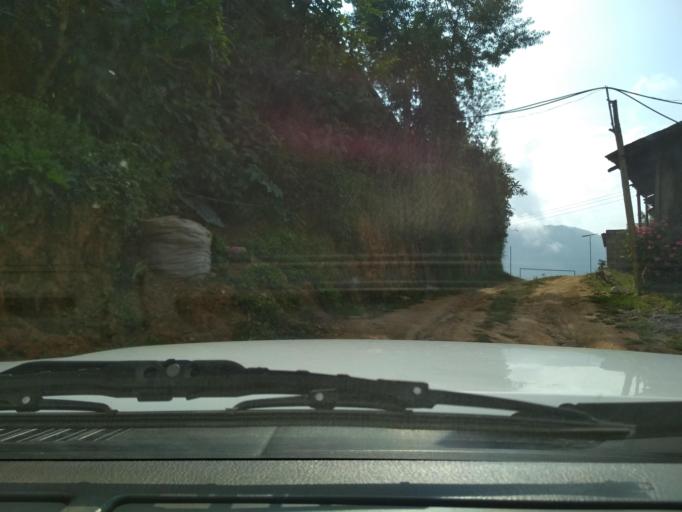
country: MX
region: Veracruz
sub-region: Soledad Atzompa
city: Tlatilpa
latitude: 18.7550
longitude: -97.1507
